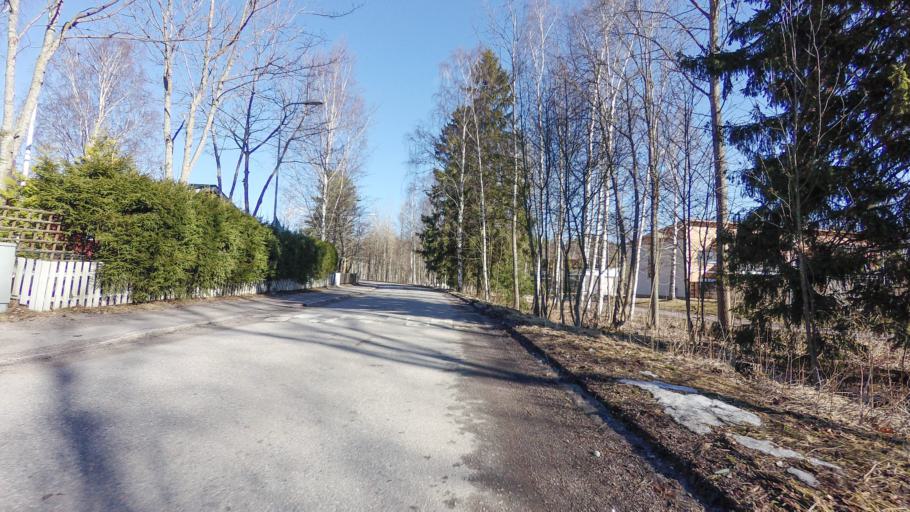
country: FI
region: Uusimaa
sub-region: Helsinki
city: Helsinki
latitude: 60.1701
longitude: 25.0553
